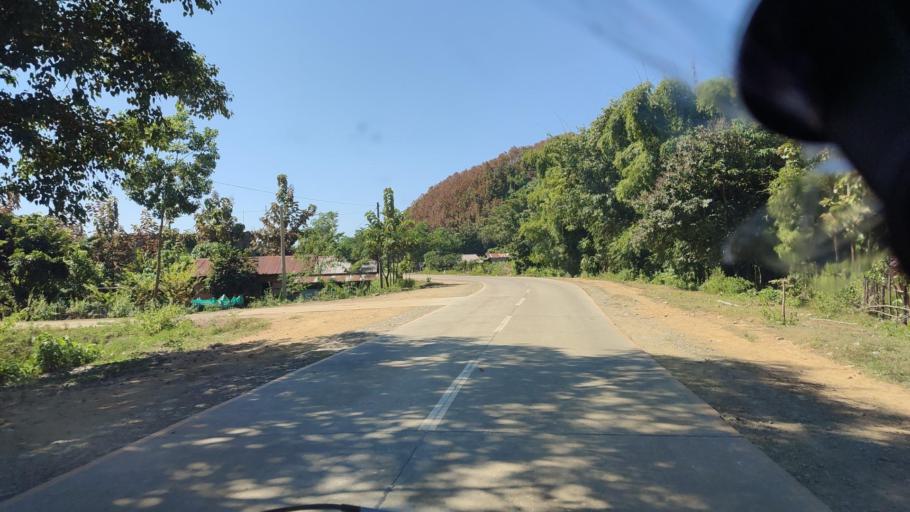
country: MM
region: Rakhine
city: Sittwe
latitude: 20.1309
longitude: 93.4604
